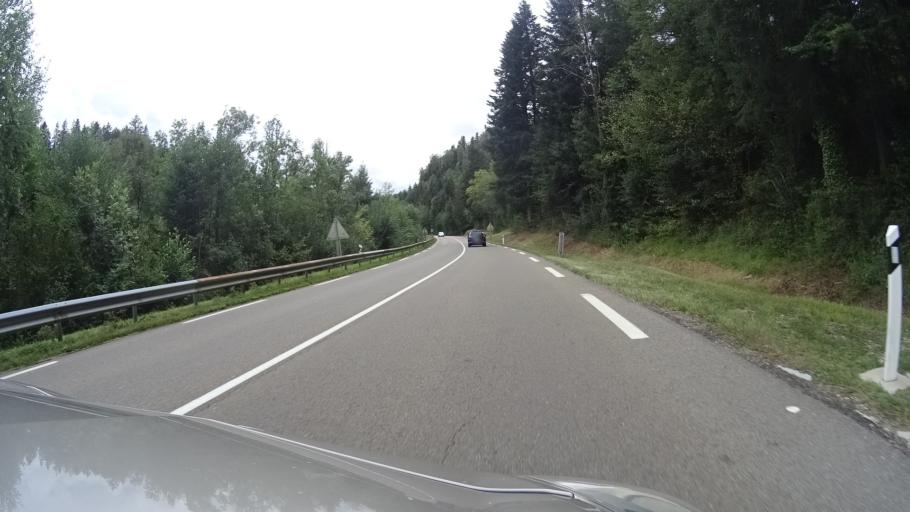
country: FR
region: Franche-Comte
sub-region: Departement du Jura
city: Champagnole
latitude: 46.6483
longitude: 5.9418
